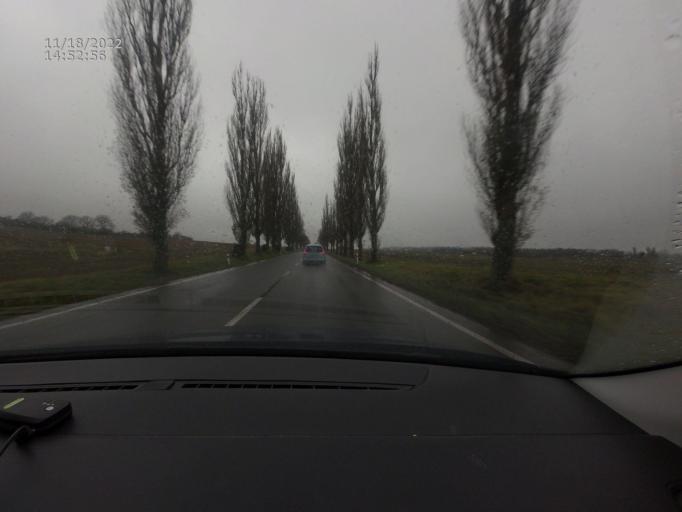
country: CZ
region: Jihocesky
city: Milevsko
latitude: 49.4538
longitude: 14.3488
